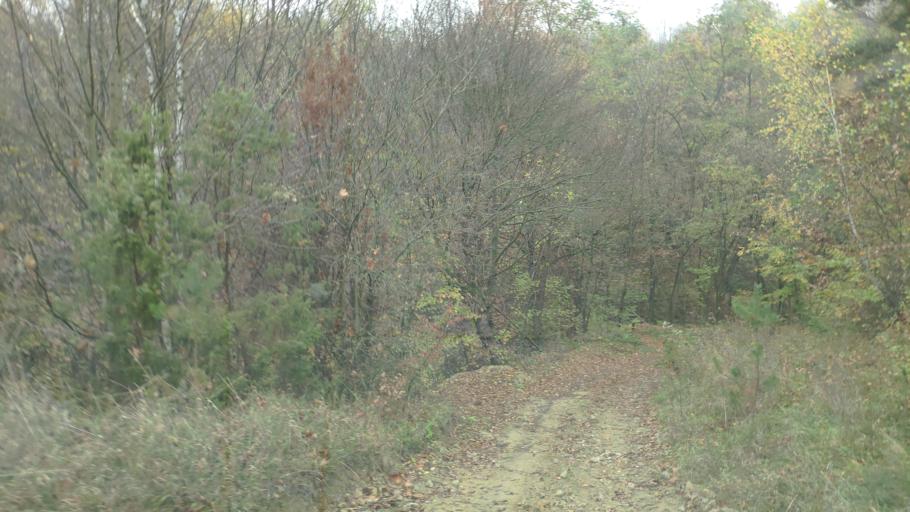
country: SK
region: Presovsky
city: Sabinov
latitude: 49.1417
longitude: 21.2194
